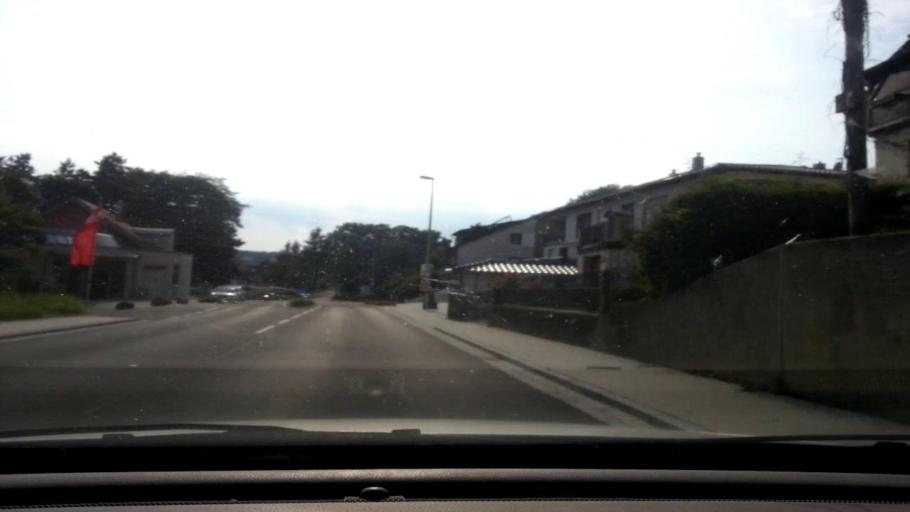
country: DE
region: Bavaria
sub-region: Upper Franconia
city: Litzendorf
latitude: 49.9119
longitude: 11.0074
